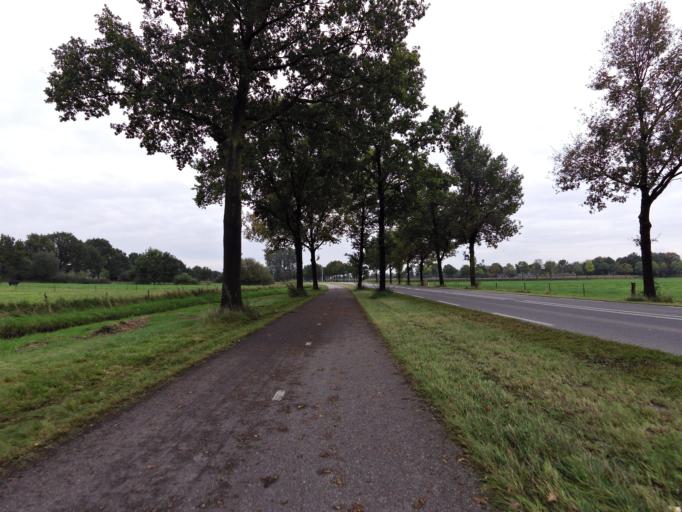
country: NL
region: Gelderland
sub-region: Oude IJsselstreek
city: Gendringen
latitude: 51.8930
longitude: 6.3619
